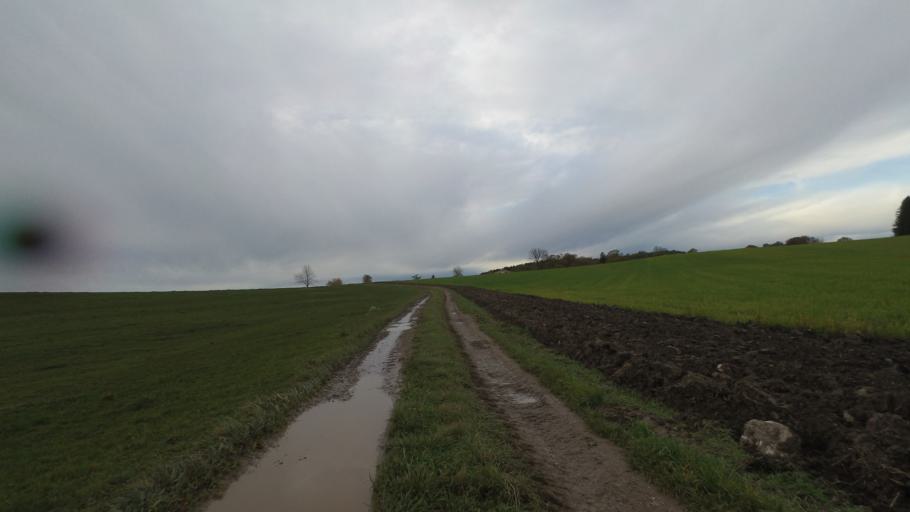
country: DE
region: Bavaria
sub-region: Upper Bavaria
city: Nussdorf
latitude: 47.9112
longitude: 12.5687
